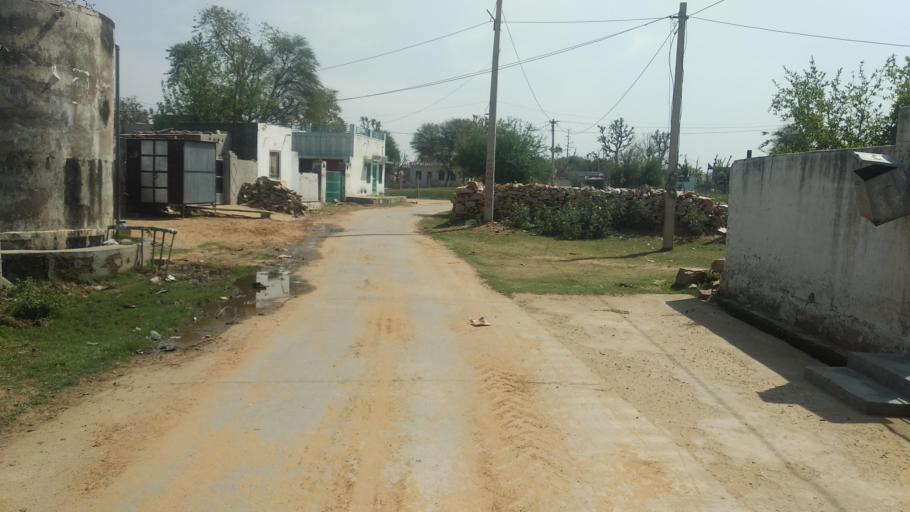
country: IN
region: Rajasthan
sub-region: Sikar
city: Sikar
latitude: 27.4673
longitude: 75.0841
